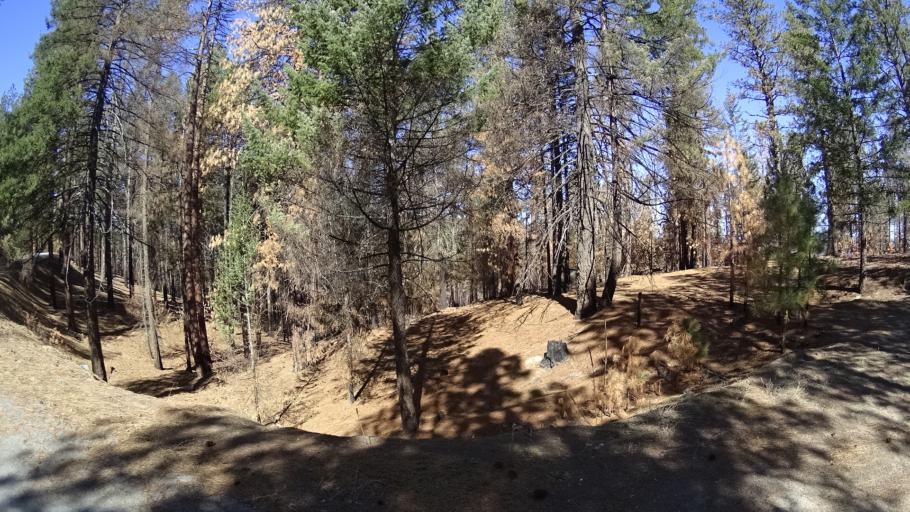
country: US
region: California
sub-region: Tehama County
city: Rancho Tehama Reserve
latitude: 39.6529
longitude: -122.7259
